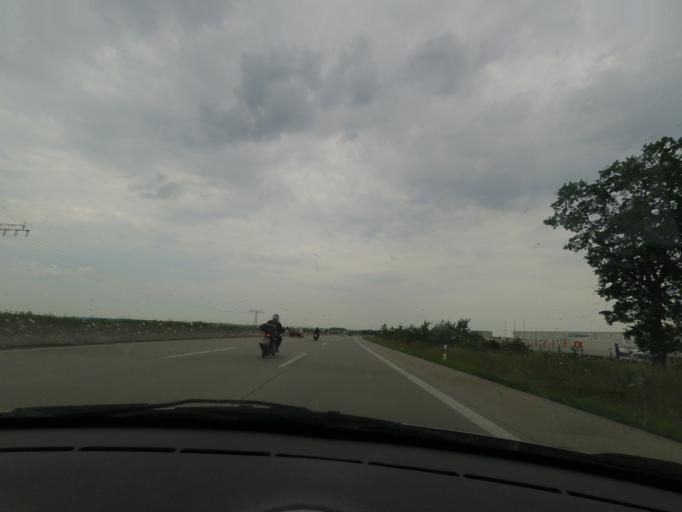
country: DE
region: Thuringia
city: Ronneburg
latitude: 50.8772
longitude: 12.1675
